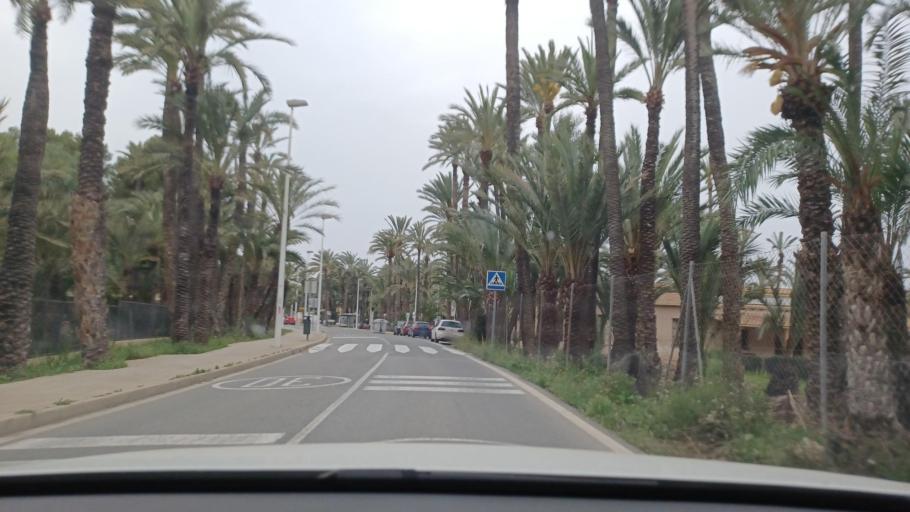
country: ES
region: Valencia
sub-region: Provincia de Alicante
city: Elche
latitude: 38.2559
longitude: -0.6921
